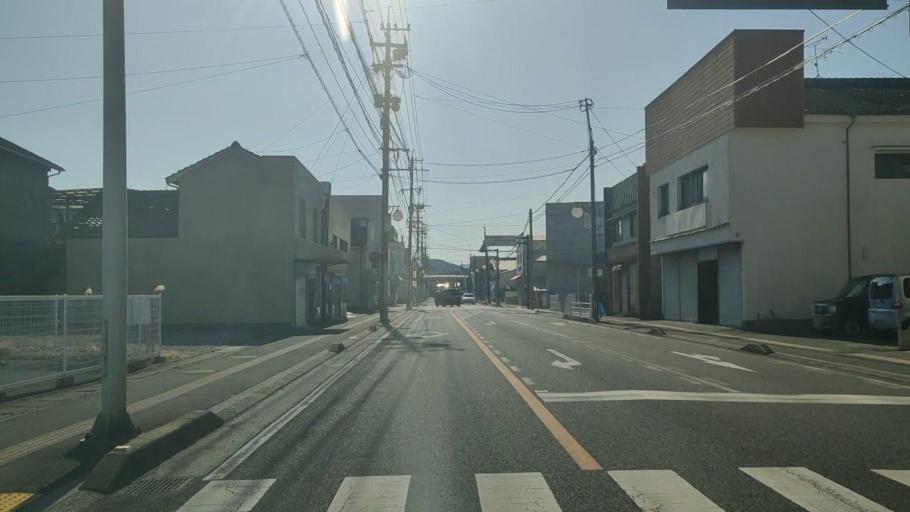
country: JP
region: Oita
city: Saiki
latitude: 32.9652
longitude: 131.9011
